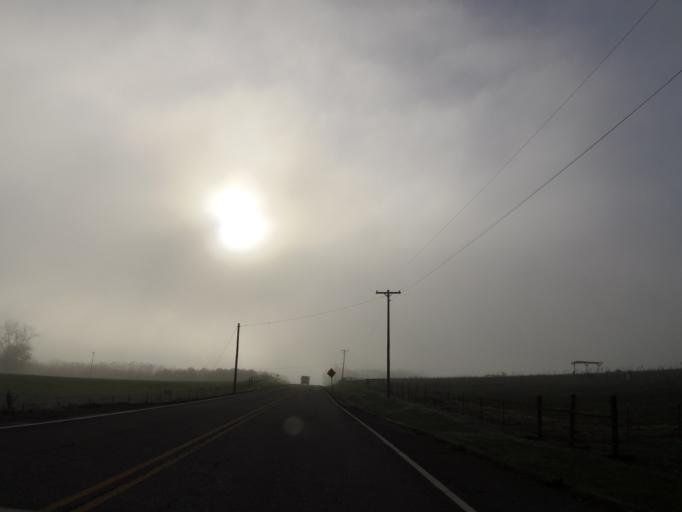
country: US
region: Tennessee
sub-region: Blount County
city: Alcoa
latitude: 35.8449
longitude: -83.9637
